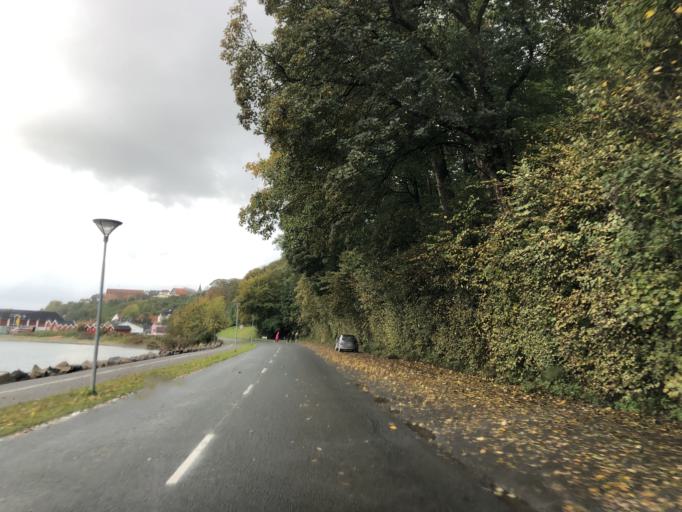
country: DK
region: Central Jutland
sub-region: Lemvig Kommune
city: Lemvig
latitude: 56.5520
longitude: 8.2972
